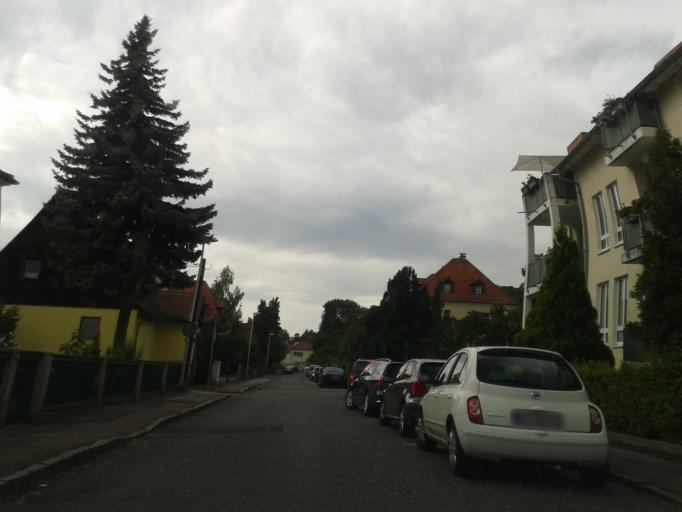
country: DE
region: Saxony
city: Radebeul
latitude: 51.1117
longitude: 13.6517
